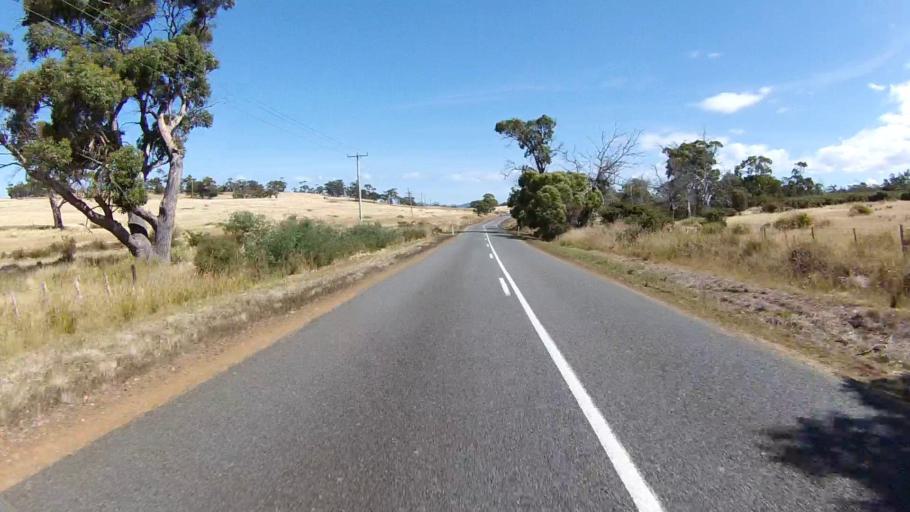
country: AU
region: Tasmania
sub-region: Sorell
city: Sorell
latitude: -42.2961
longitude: 147.9870
